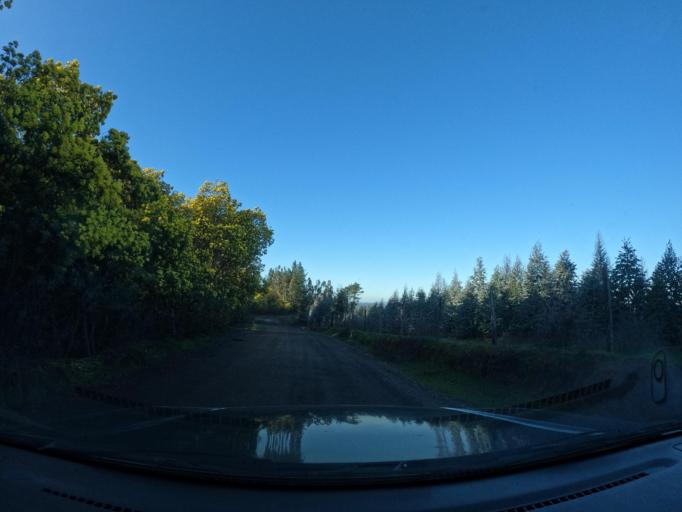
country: CL
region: Biobio
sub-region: Provincia de Concepcion
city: Chiguayante
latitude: -37.0169
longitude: -72.8515
